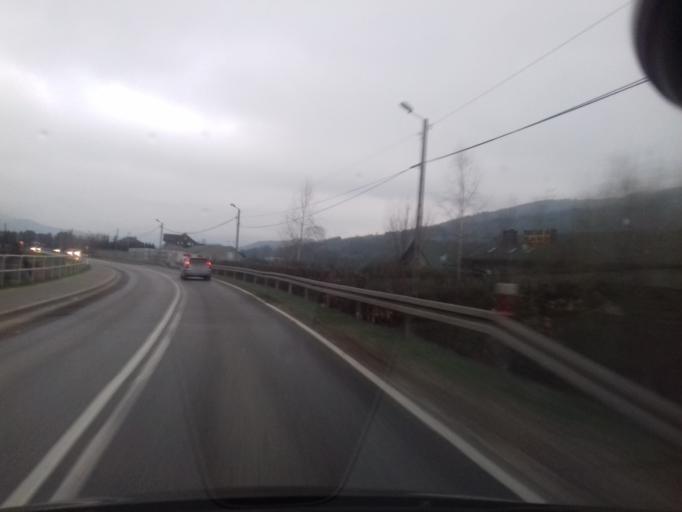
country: PL
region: Lesser Poland Voivodeship
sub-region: Powiat myslenicki
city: Lubien
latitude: 49.7054
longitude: 20.0285
